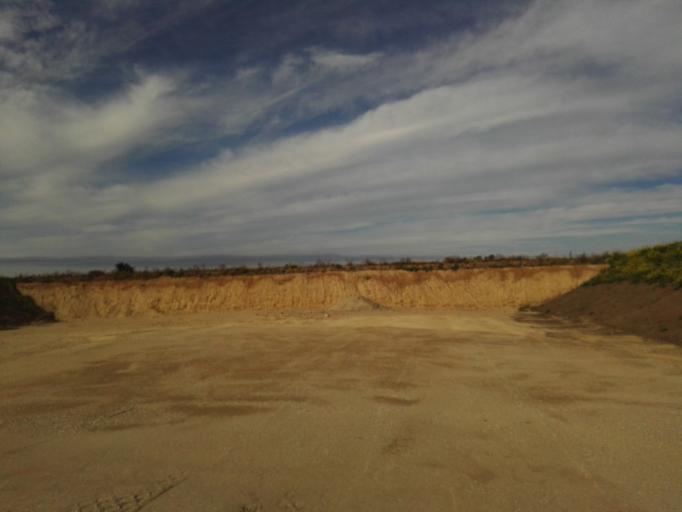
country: DK
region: Capital Region
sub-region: Frederikssund Kommune
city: Frederikssund
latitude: 55.8129
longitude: 12.0834
